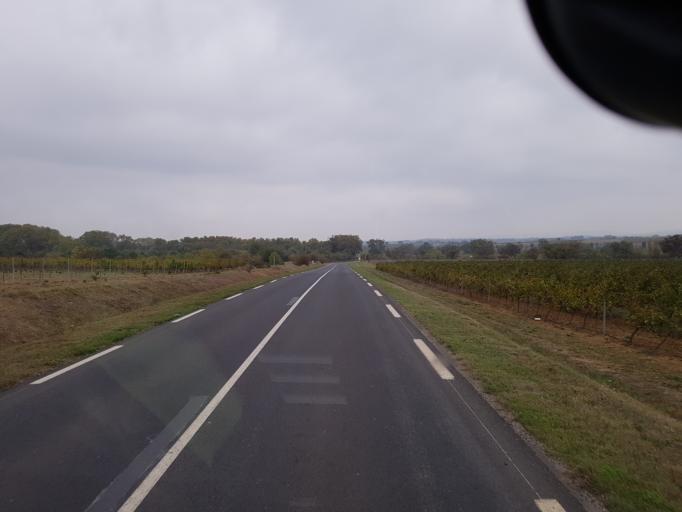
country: FR
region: Languedoc-Roussillon
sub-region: Departement de l'Herault
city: Pinet
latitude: 43.3998
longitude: 3.5390
